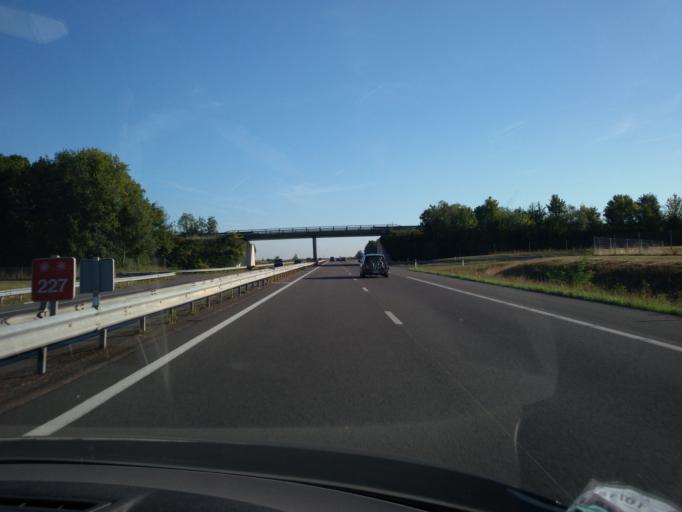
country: FR
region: Centre
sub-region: Departement du Cher
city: Levet
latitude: 46.9178
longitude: 2.4230
